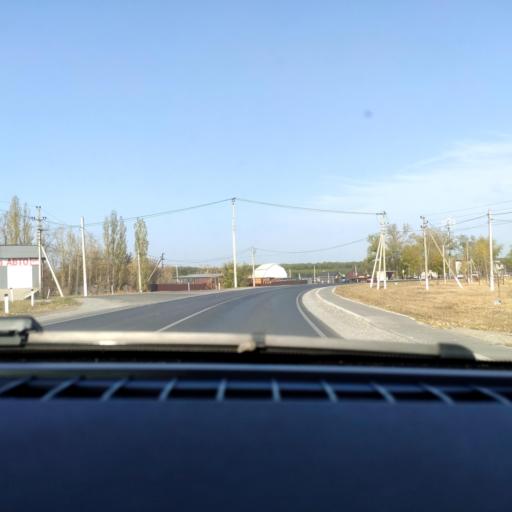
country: RU
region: Voronezj
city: Novaya Usman'
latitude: 51.6599
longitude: 39.4011
